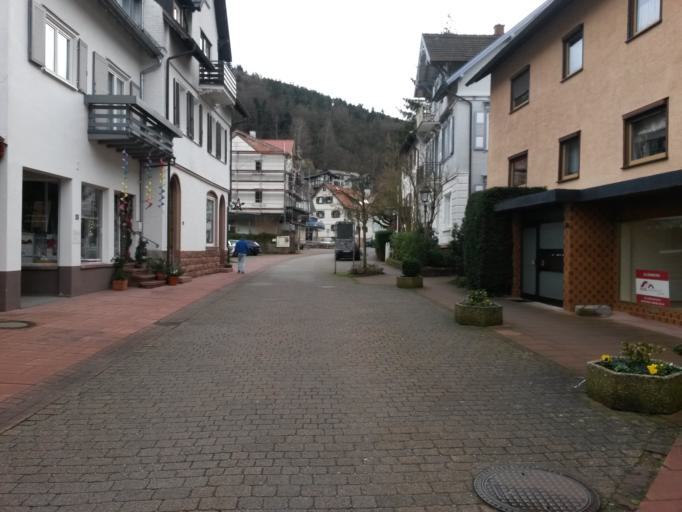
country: DE
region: Baden-Wuerttemberg
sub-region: Karlsruhe Region
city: Bad Herrenalb
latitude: 48.7958
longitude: 8.4372
